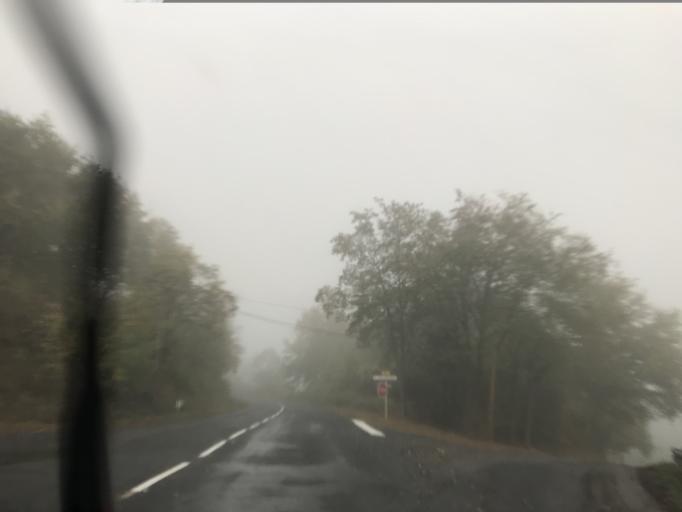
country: FR
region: Auvergne
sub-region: Departement du Puy-de-Dome
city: Escoutoux
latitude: 45.7860
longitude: 3.6052
